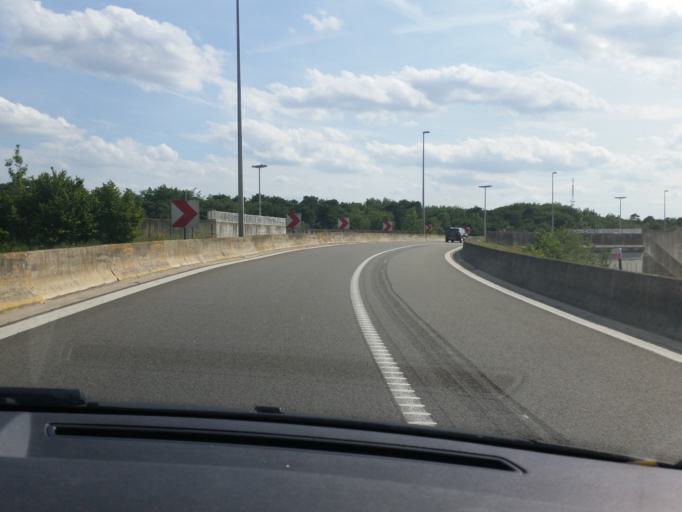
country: BE
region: Flanders
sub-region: Provincie Antwerpen
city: Brasschaat
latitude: 51.3078
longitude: 4.5525
